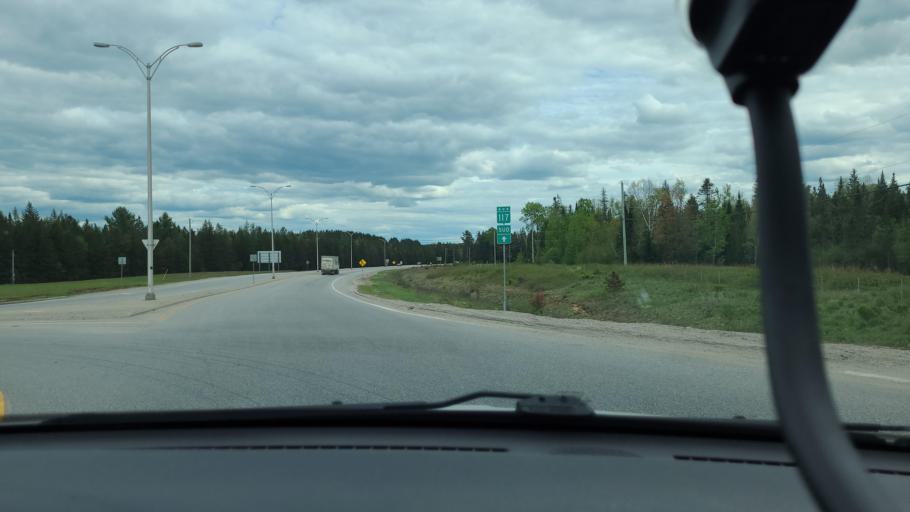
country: CA
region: Quebec
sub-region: Laurentides
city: Riviere-Rouge
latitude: 46.3908
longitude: -74.8623
